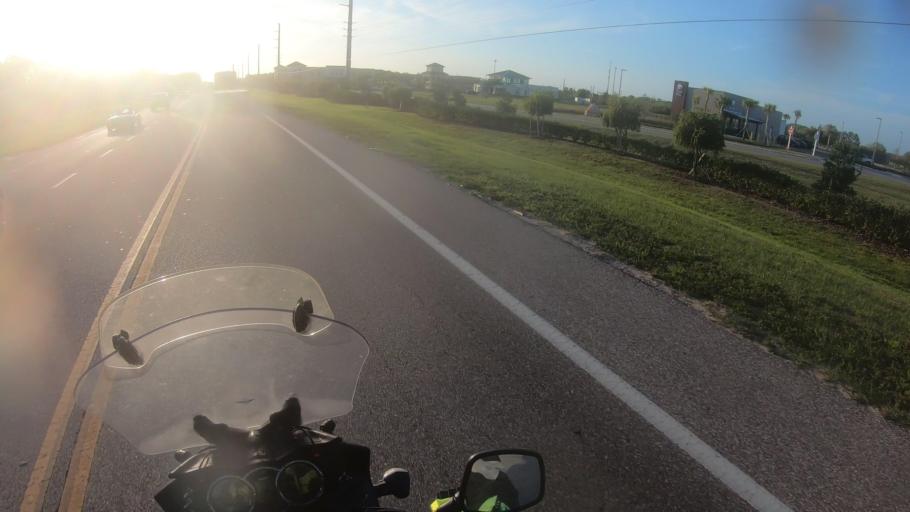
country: US
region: Florida
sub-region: Sarasota County
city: The Meadows
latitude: 27.4320
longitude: -82.3865
